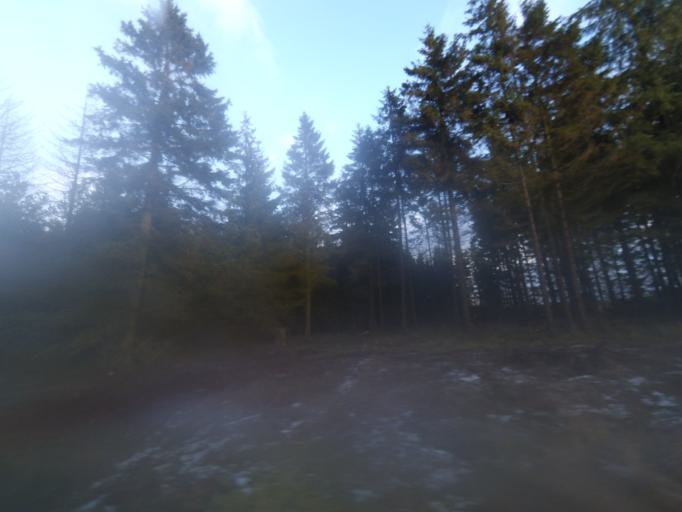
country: DK
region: Central Jutland
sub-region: Ikast-Brande Kommune
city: Brande
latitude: 56.0144
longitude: 9.1629
